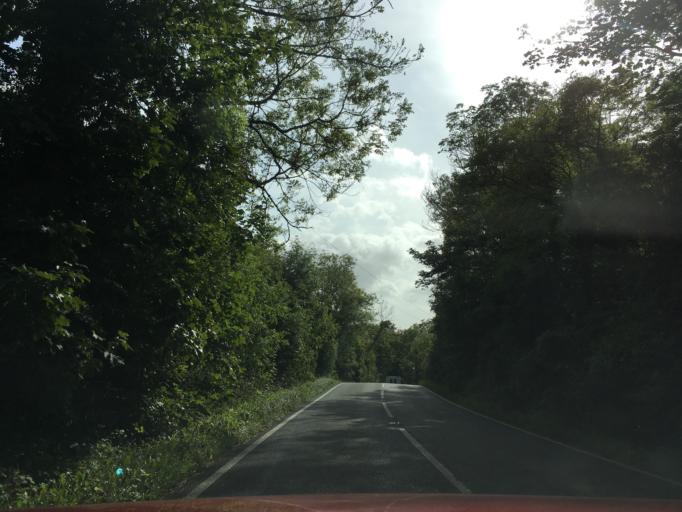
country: GB
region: England
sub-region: Gloucestershire
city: Stonehouse
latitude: 51.7177
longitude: -2.2774
